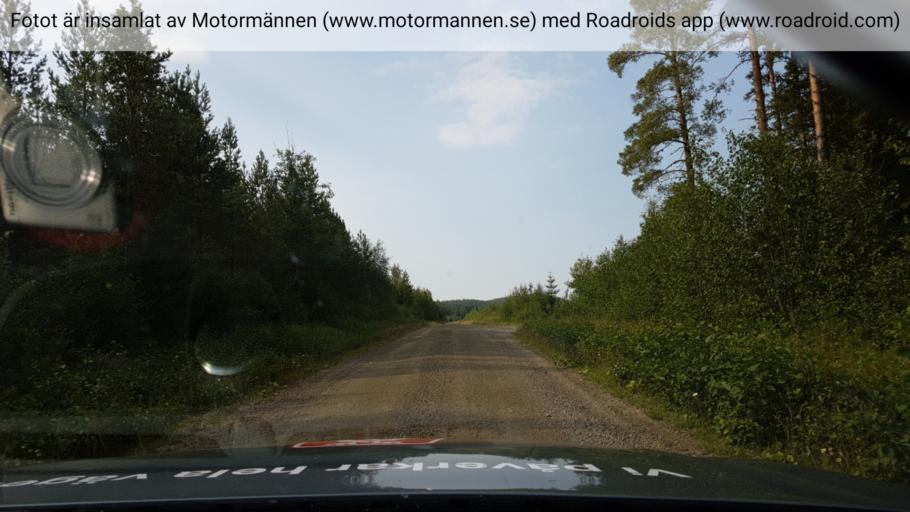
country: SE
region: Jaemtland
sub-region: Bergs Kommun
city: Hoverberg
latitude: 62.5389
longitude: 14.9061
